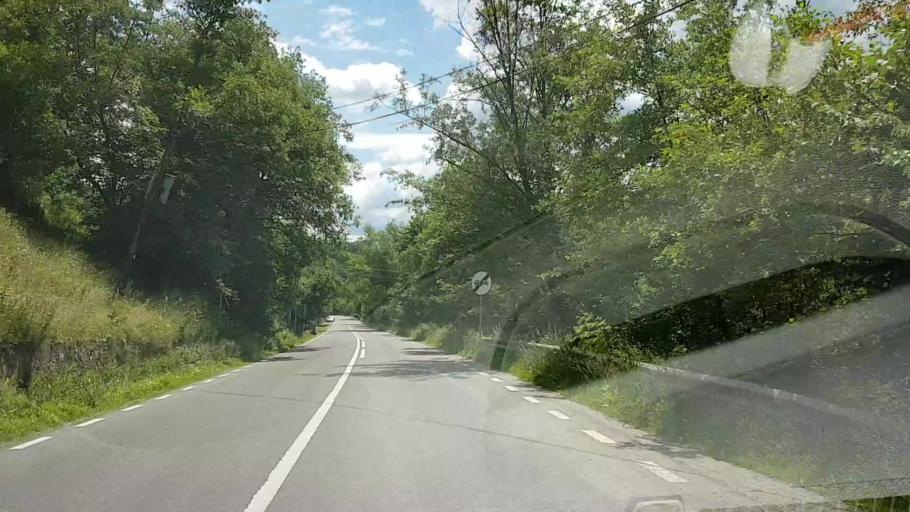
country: RO
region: Suceava
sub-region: Comuna Brosteni
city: Brosteni
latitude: 47.2587
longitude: 25.6904
